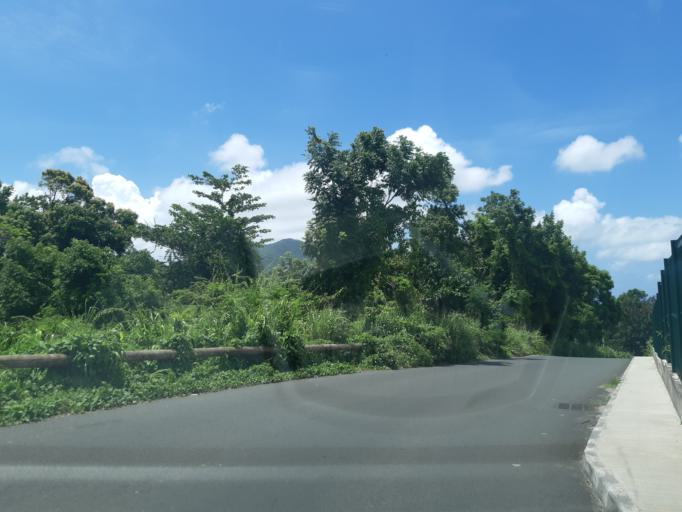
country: GP
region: Guadeloupe
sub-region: Guadeloupe
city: Basse-Terre
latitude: 16.0074
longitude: -61.7150
